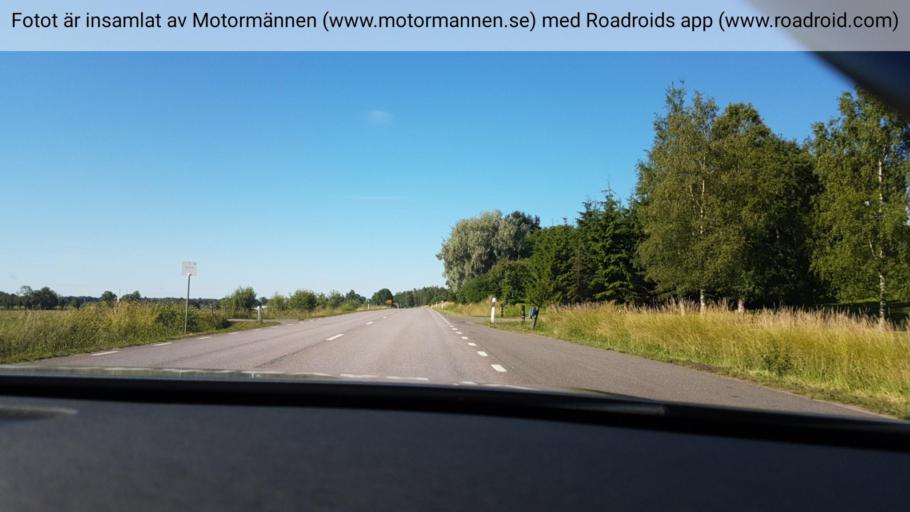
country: SE
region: Vaestra Goetaland
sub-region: Falkopings Kommun
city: Falkoeping
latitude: 58.1020
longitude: 13.5318
